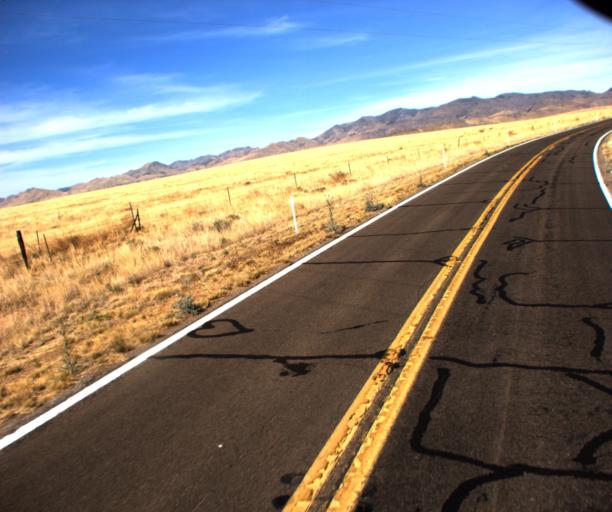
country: US
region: Arizona
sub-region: Cochise County
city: Willcox
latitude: 31.9920
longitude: -109.4486
